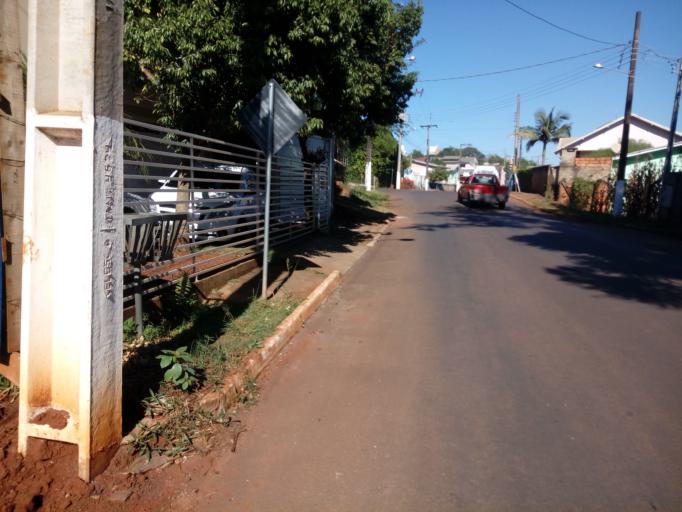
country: BR
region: Santa Catarina
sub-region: Chapeco
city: Chapeco
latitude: -27.0631
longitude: -52.6041
